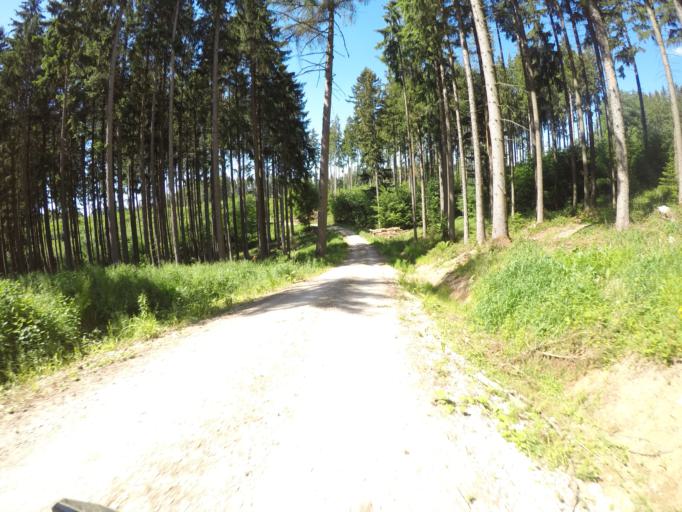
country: DE
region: Bavaria
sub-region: Lower Bavaria
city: Kumhausen
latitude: 48.5077
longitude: 12.1916
